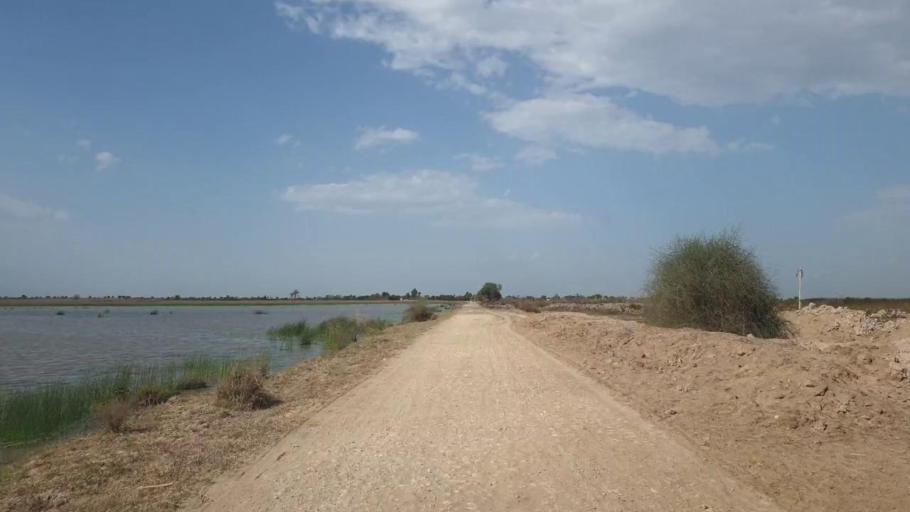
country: PK
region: Sindh
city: Shahdadpur
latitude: 25.9975
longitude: 68.4624
